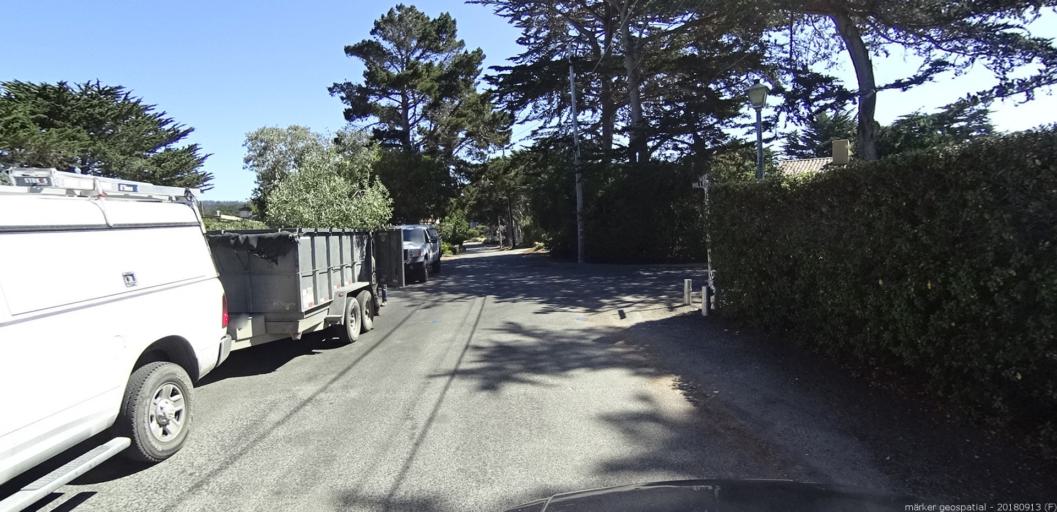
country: US
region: California
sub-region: Monterey County
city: Carmel-by-the-Sea
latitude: 36.5433
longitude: -121.9307
